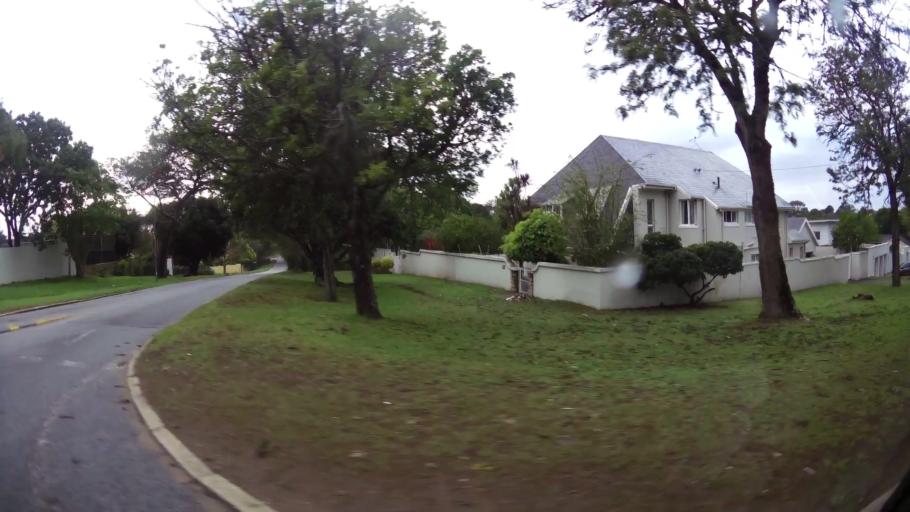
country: ZA
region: Eastern Cape
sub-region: Nelson Mandela Bay Metropolitan Municipality
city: Port Elizabeth
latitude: -33.9767
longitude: 25.5815
